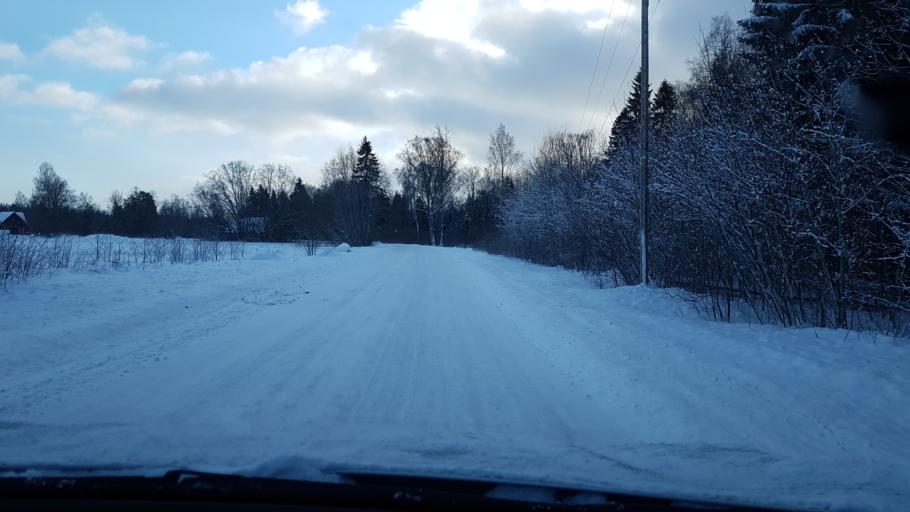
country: EE
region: Harju
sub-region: Nissi vald
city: Turba
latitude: 59.1542
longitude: 24.1448
